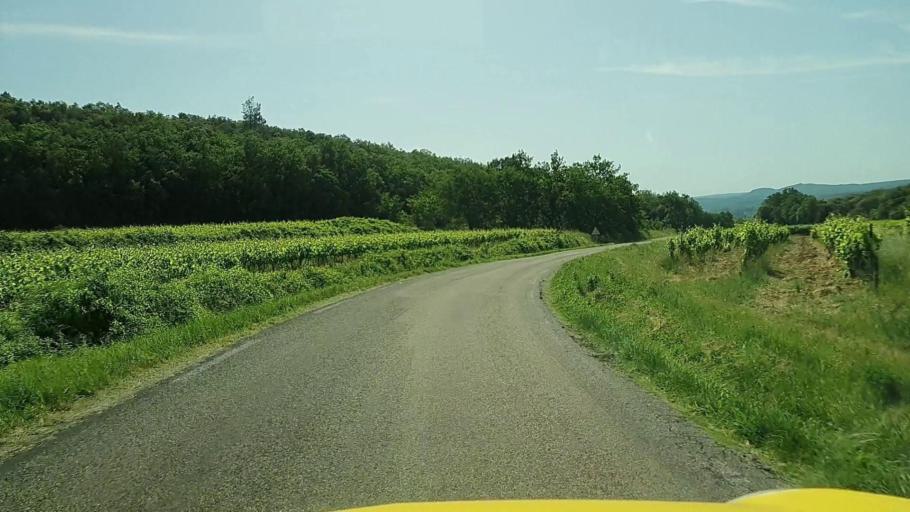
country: FR
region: Languedoc-Roussillon
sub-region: Departement du Gard
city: Sabran
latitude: 44.1298
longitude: 4.4950
